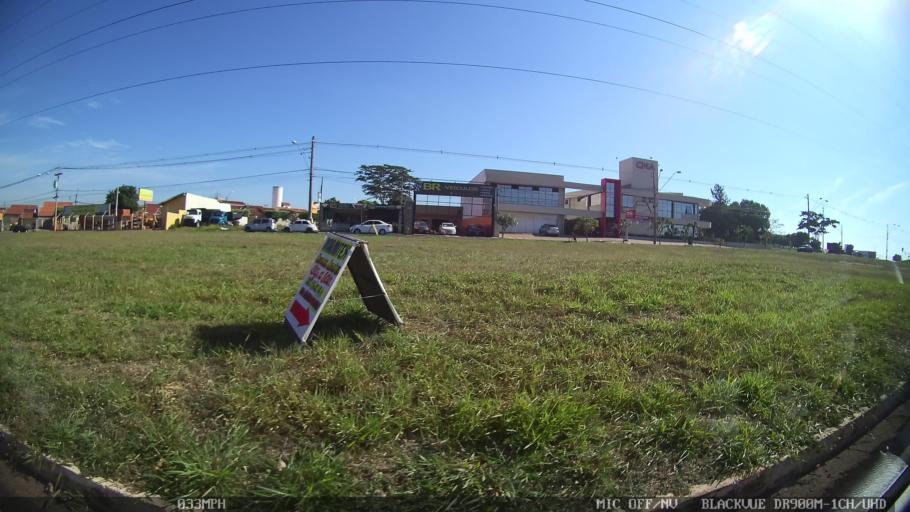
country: BR
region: Sao Paulo
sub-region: Sao Jose Do Rio Preto
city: Sao Jose do Rio Preto
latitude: -20.7702
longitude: -49.3903
